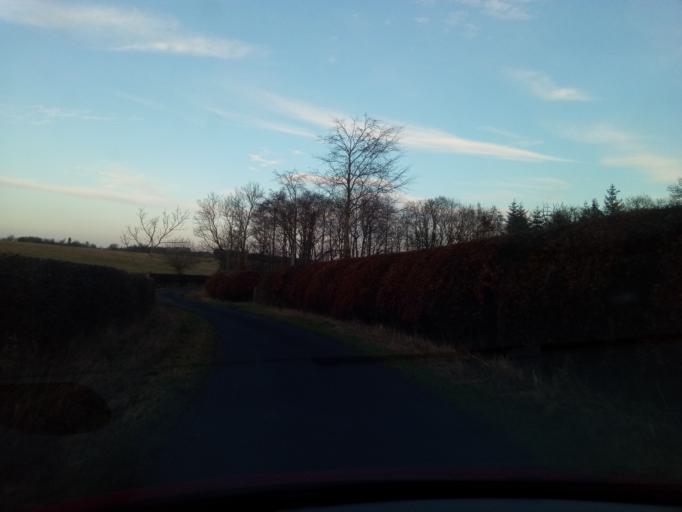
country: GB
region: Scotland
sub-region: The Scottish Borders
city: Saint Boswells
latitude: 55.5214
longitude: -2.6674
